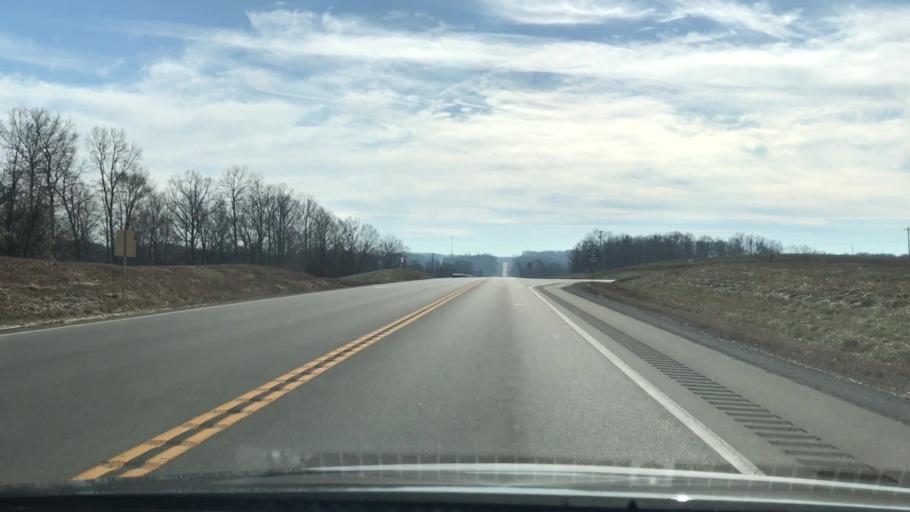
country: US
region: Kentucky
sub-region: Monroe County
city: Tompkinsville
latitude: 36.8162
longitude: -85.6883
